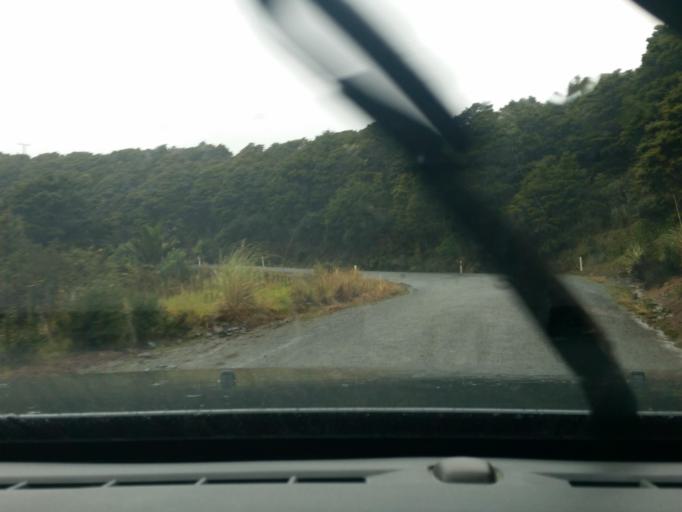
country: NZ
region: Northland
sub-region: Kaipara District
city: Dargaville
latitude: -35.7636
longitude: 173.6091
